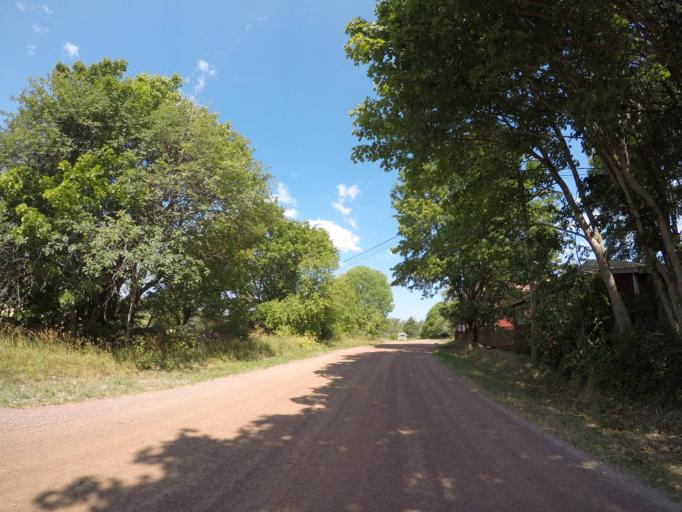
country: AX
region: Alands landsbygd
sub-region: Finstroem
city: Finstroem
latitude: 60.2148
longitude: 19.8557
